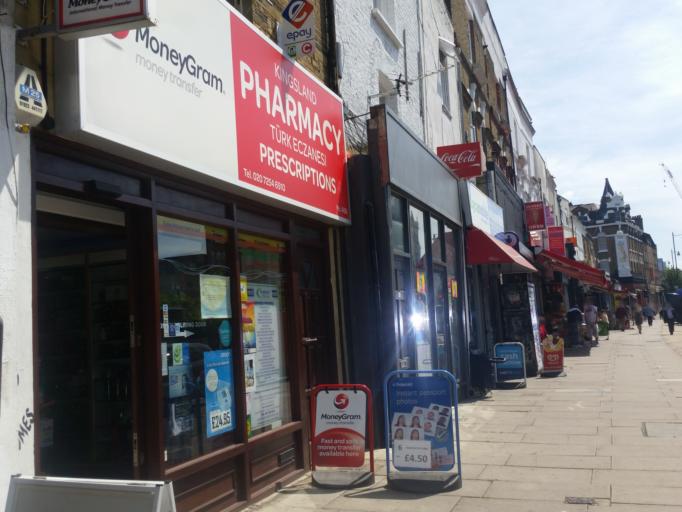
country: GB
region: England
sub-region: Greater London
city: Bethnal Green
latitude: 51.5416
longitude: -0.0762
